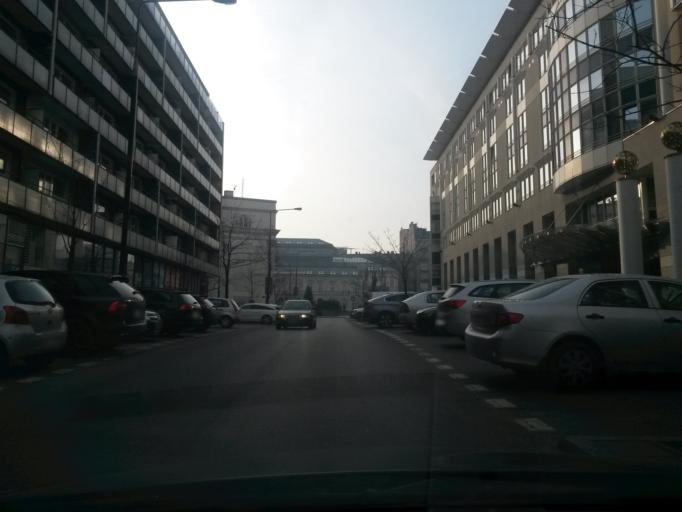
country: PL
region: Masovian Voivodeship
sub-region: Warszawa
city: Srodmiescie
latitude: 52.2278
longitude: 21.0254
